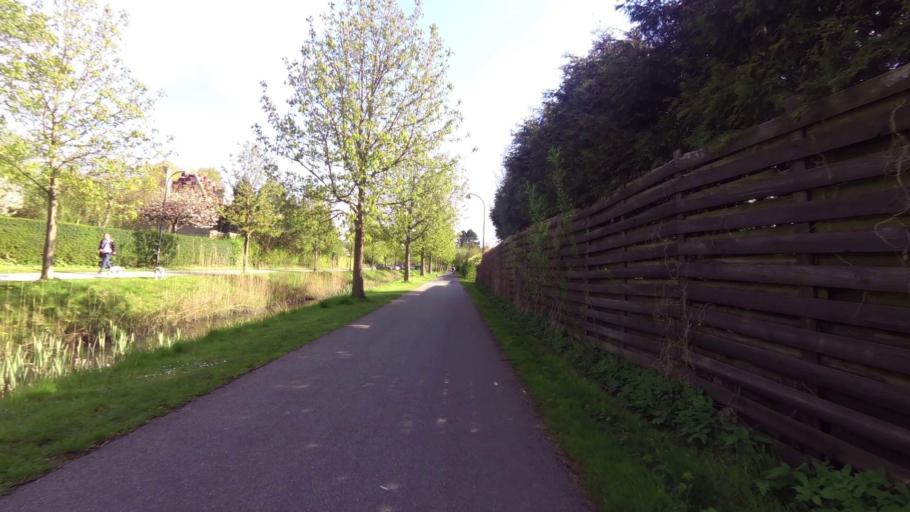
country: DK
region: Capital Region
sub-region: Lyngby-Tarbaek Kommune
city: Kongens Lyngby
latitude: 55.7338
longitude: 12.5343
